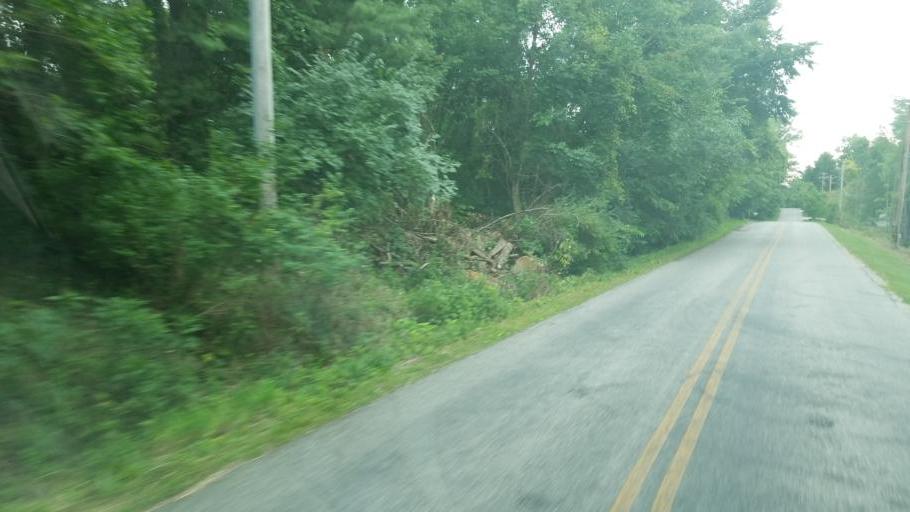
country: US
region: Ohio
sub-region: Delaware County
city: Sunbury
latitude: 40.2887
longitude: -82.8749
